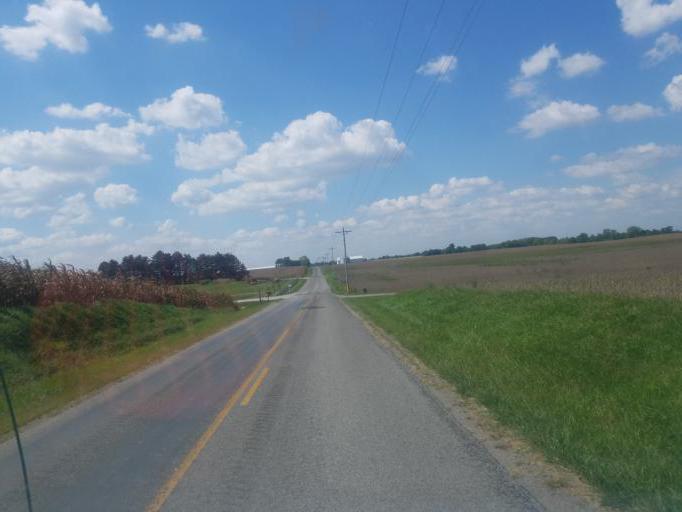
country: US
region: Ohio
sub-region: Hardin County
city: Ada
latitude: 40.6525
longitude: -83.8656
